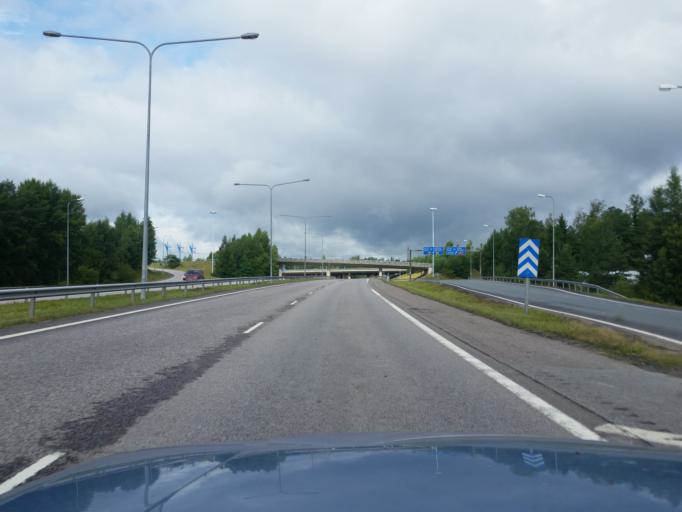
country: FI
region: Uusimaa
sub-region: Helsinki
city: Espoo
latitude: 60.2178
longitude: 24.6530
